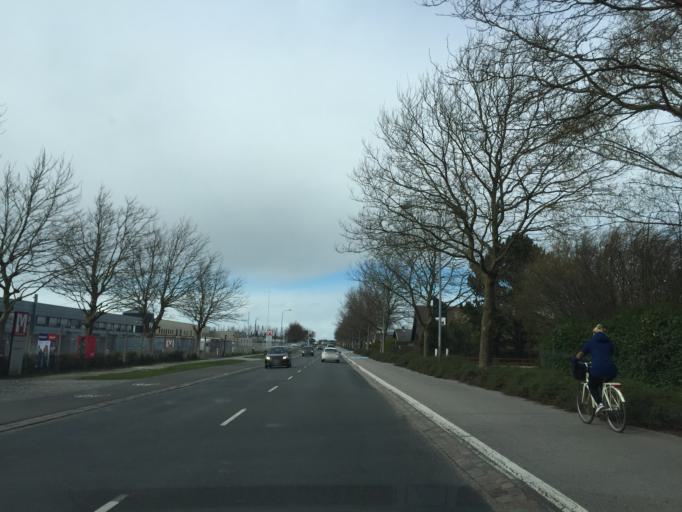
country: DK
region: South Denmark
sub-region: Odense Kommune
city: Neder Holluf
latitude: 55.3862
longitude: 10.4404
